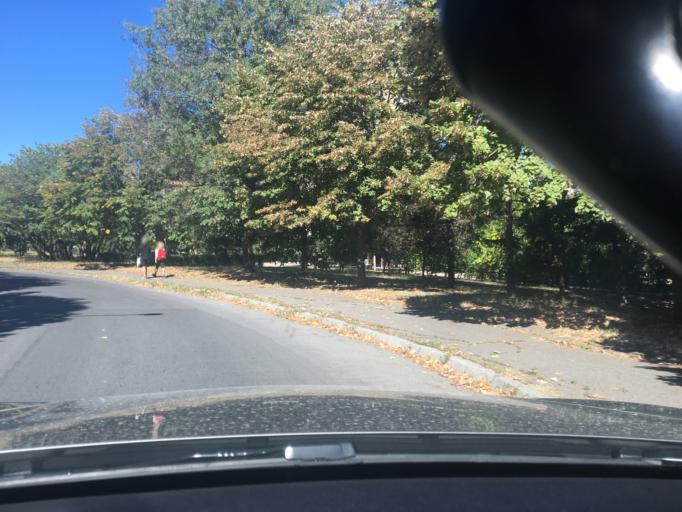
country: BG
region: Burgas
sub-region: Obshtina Burgas
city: Burgas
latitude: 42.5256
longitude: 27.4672
